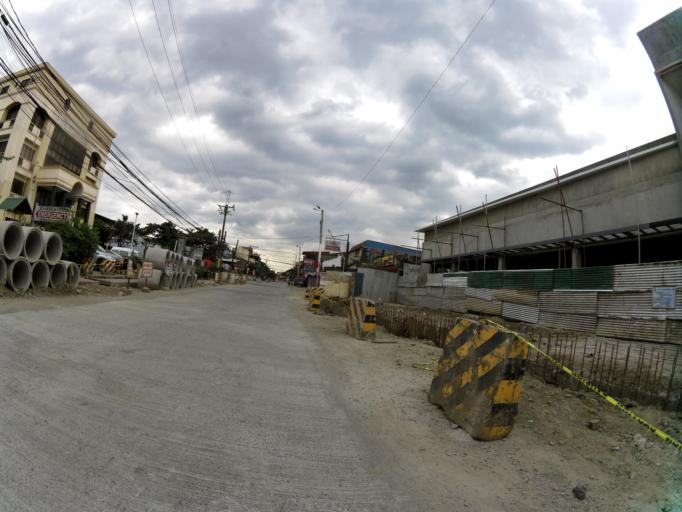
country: PH
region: Calabarzon
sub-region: Province of Rizal
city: Antipolo
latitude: 14.6398
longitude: 121.1098
